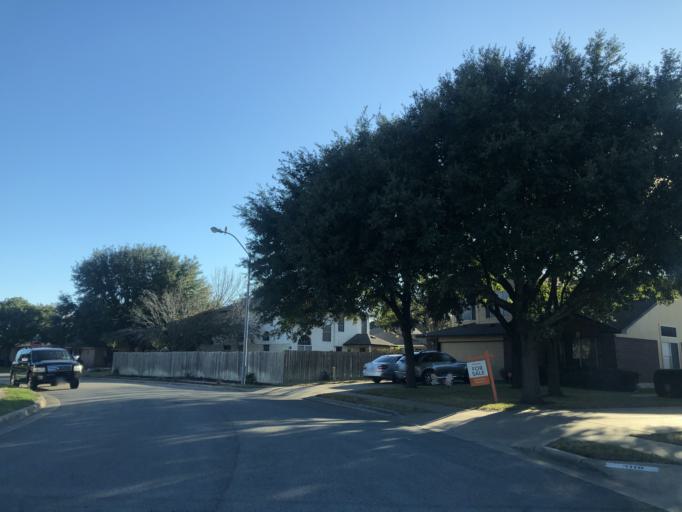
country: US
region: Texas
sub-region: Travis County
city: Windemere
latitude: 30.4800
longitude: -97.6571
